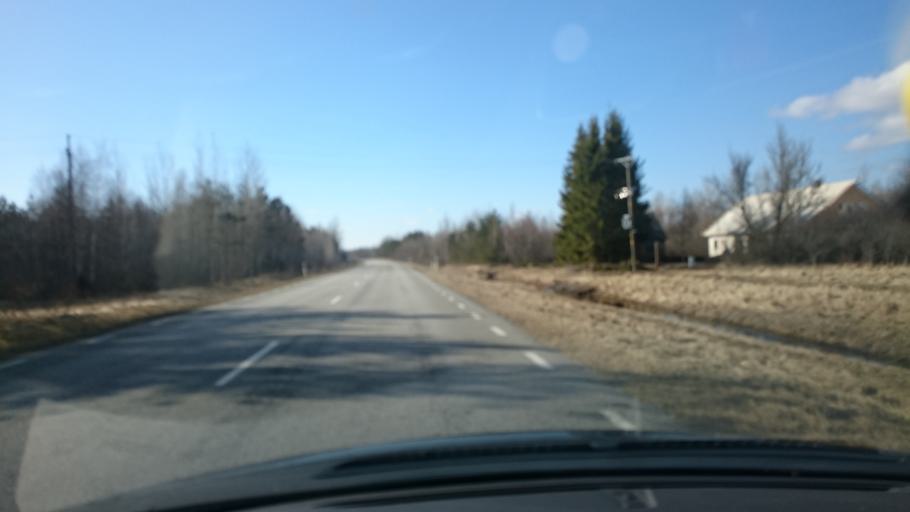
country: EE
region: Laeaene
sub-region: Lihula vald
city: Lihula
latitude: 58.6204
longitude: 23.9047
